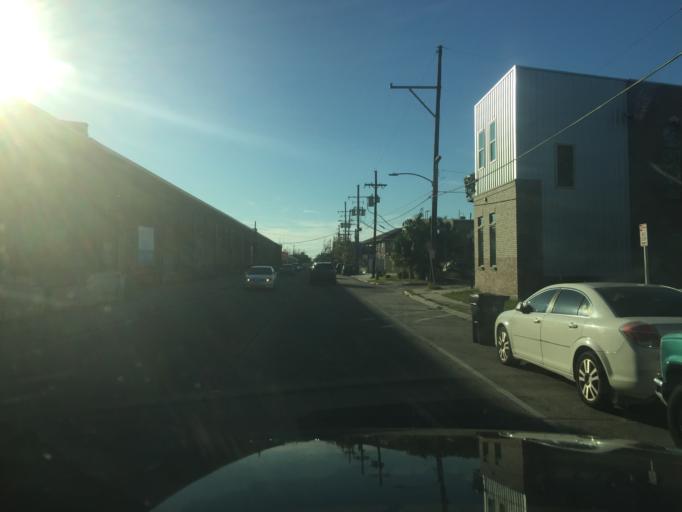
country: US
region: Louisiana
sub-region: Jefferson Parish
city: Harvey
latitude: 29.9179
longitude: -90.0918
